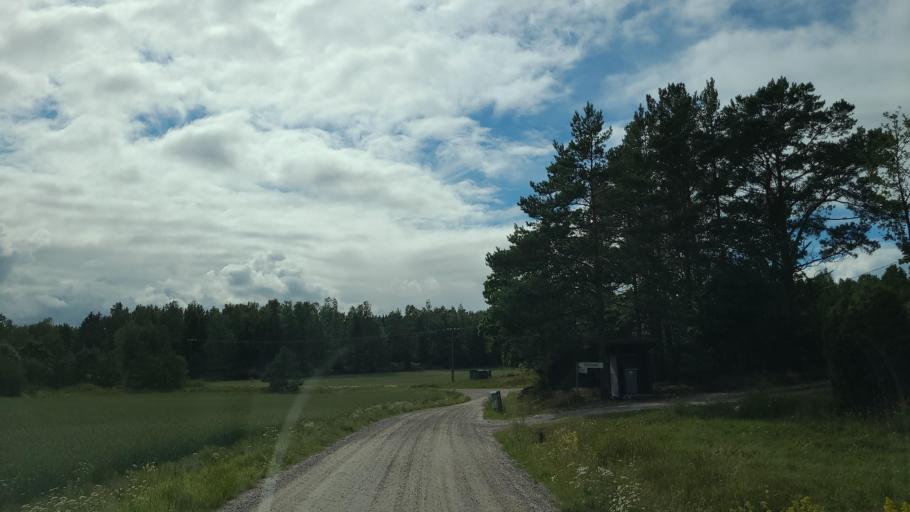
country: FI
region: Varsinais-Suomi
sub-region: Aboland-Turunmaa
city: Nagu
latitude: 60.1956
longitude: 21.7708
